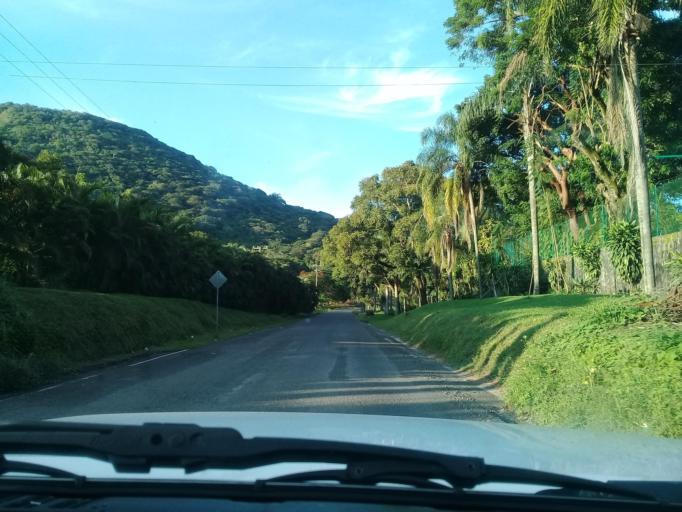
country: MX
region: Veracruz
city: Catemaco
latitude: 18.4262
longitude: -95.0949
